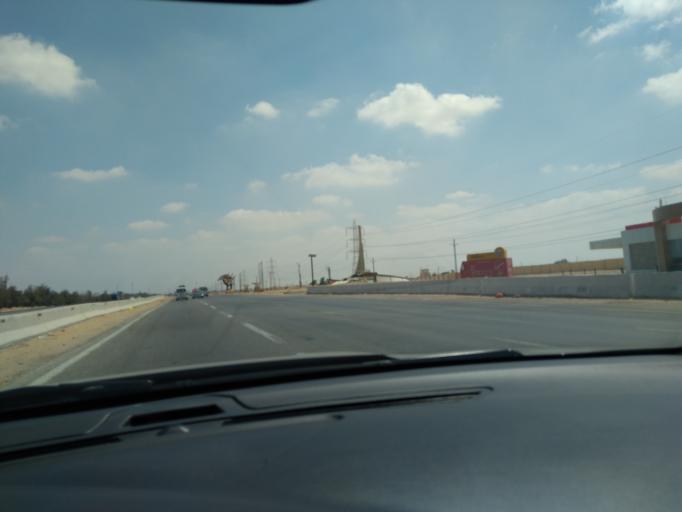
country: EG
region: Al Isma'iliyah
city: At Tall al Kabir
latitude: 30.3983
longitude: 31.9812
